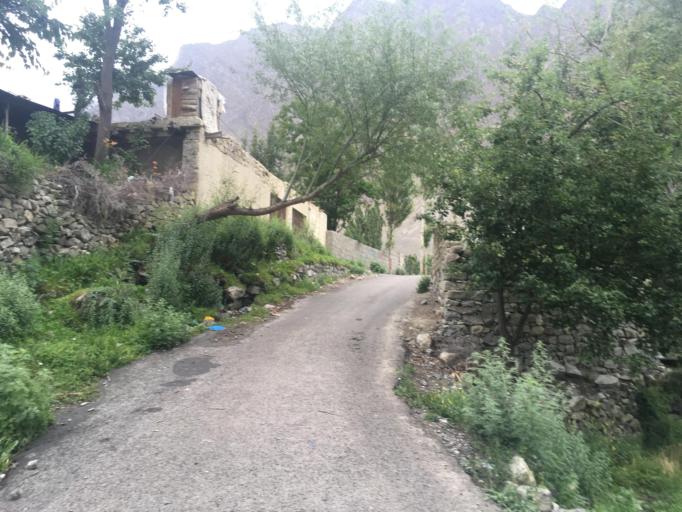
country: PK
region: Gilgit-Baltistan
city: Skardu
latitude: 35.2663
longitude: 75.6344
